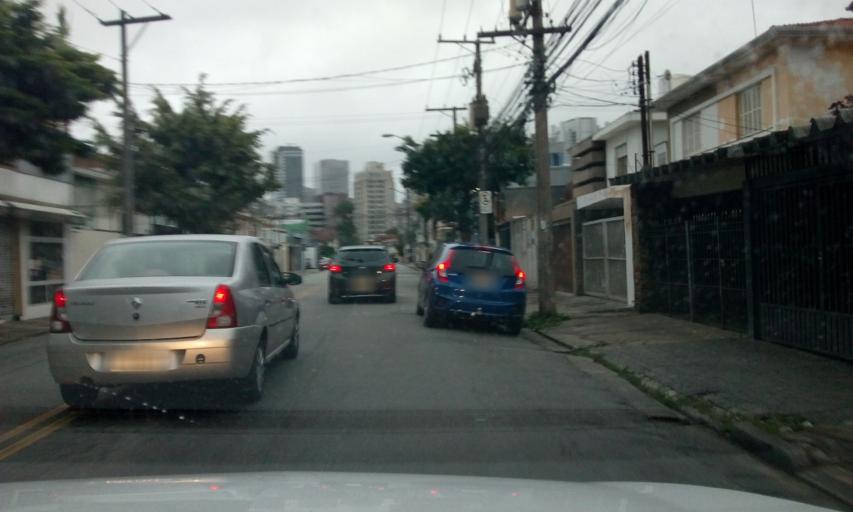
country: BR
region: Sao Paulo
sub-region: Sao Paulo
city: Sao Paulo
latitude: -23.6014
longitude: -46.6894
